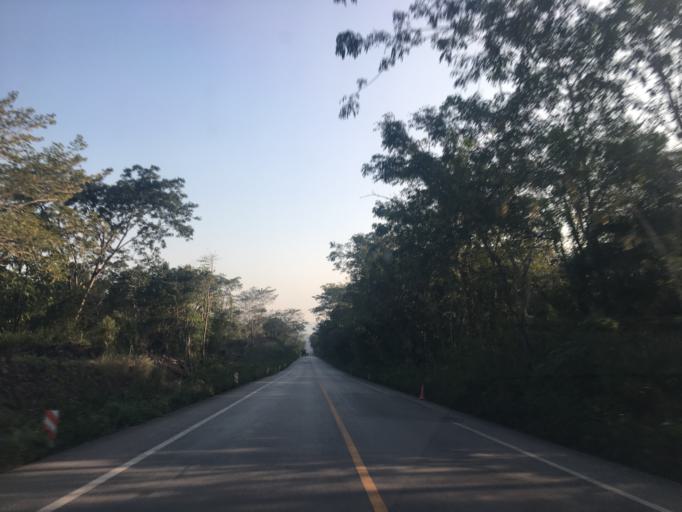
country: TH
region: Lampang
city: Ngao
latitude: 18.6581
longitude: 100.0176
